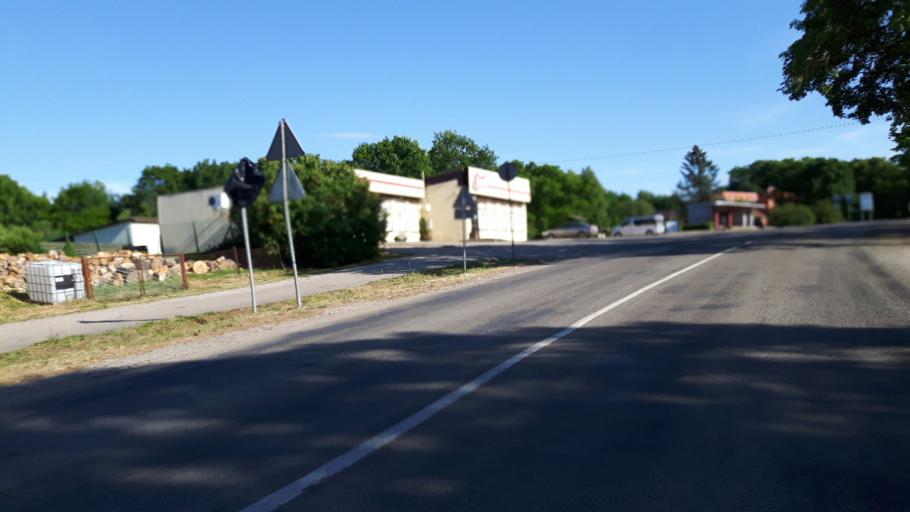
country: LV
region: Talsu Rajons
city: Stende
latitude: 57.0690
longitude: 22.2934
